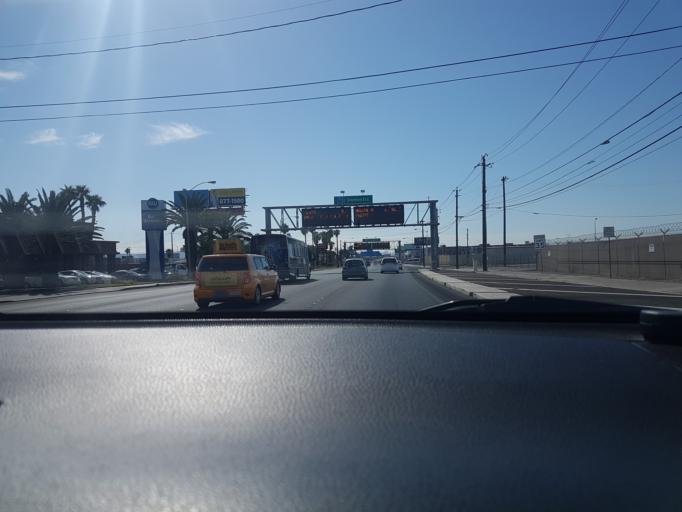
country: US
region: Nevada
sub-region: Clark County
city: Paradise
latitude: 36.1003
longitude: -115.1493
